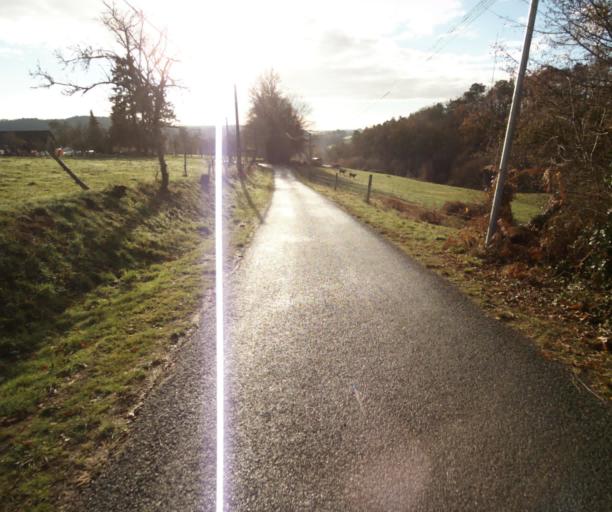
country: FR
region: Limousin
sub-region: Departement de la Correze
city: Saint-Mexant
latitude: 45.2508
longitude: 1.6330
